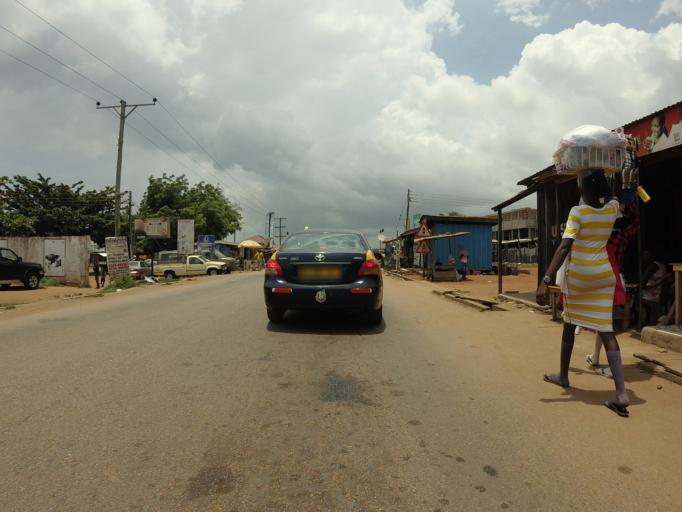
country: GH
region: Greater Accra
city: Medina Estates
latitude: 5.6864
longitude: -0.1703
